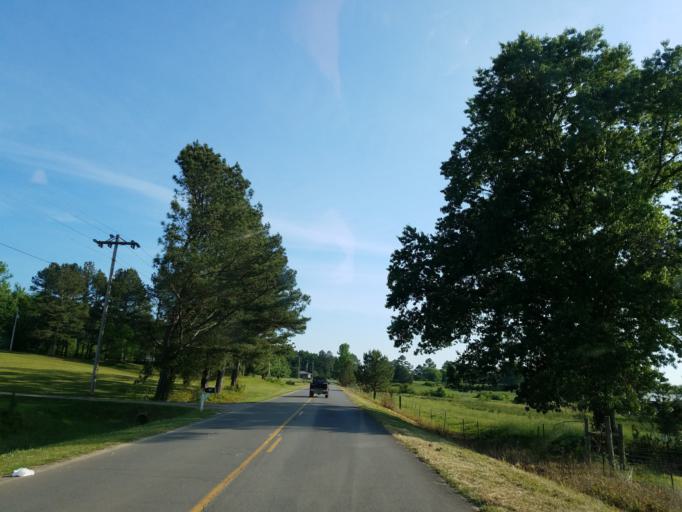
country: US
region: Georgia
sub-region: Chattooga County
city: Trion
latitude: 34.5729
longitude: -85.1550
